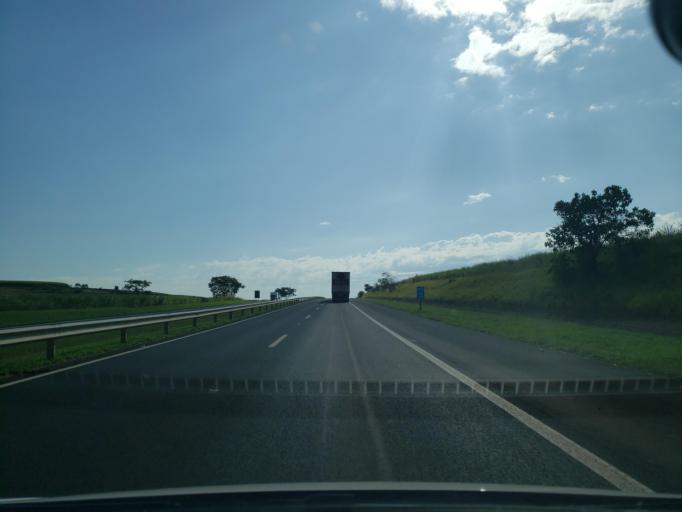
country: BR
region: Sao Paulo
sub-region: Promissao
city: Promissao
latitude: -21.5453
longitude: -49.9638
